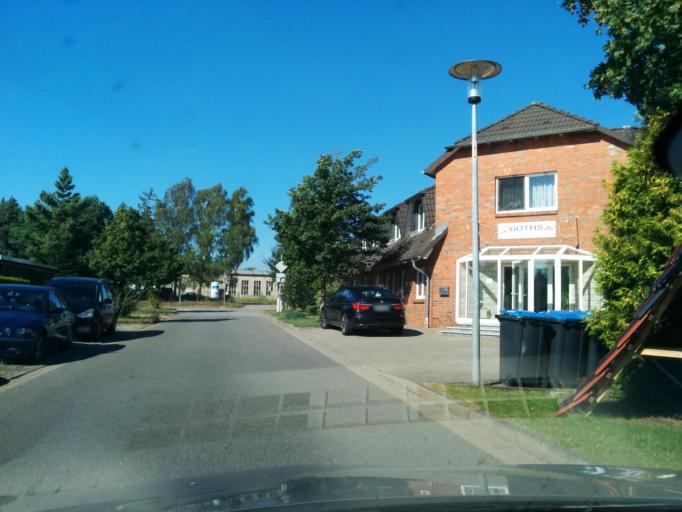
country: DE
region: Mecklenburg-Vorpommern
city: Torgelow
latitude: 53.6324
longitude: 13.9985
